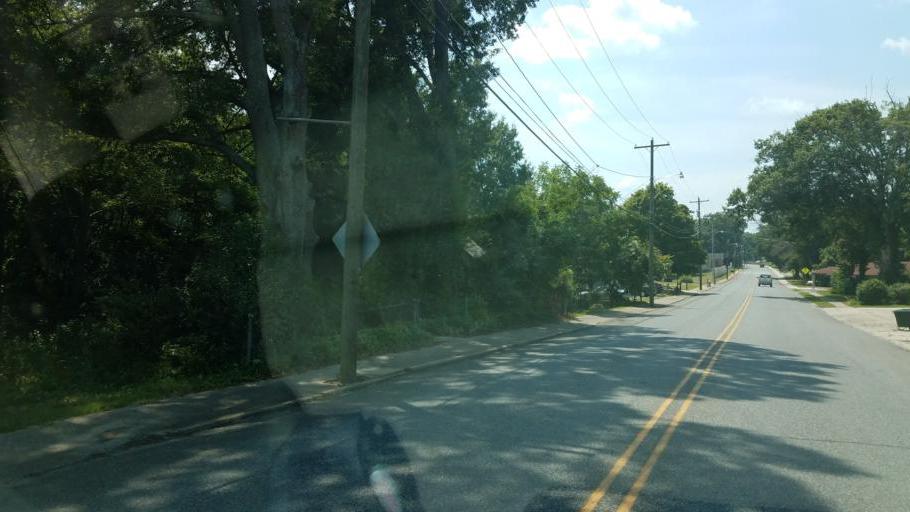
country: US
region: North Carolina
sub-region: Gaston County
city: Cherryville
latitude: 35.3757
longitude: -81.3784
